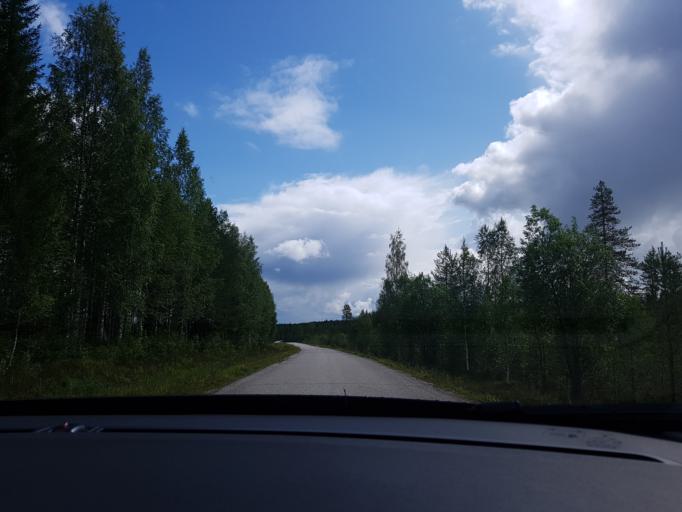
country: FI
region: Kainuu
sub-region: Kehys-Kainuu
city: Kuhmo
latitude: 64.4513
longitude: 29.6692
